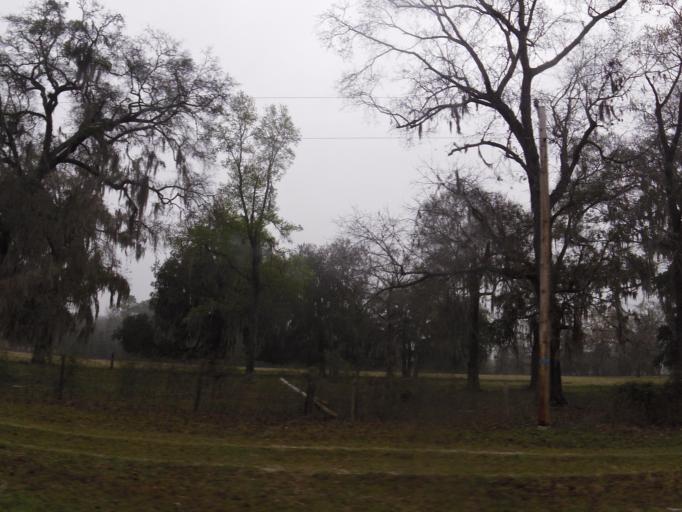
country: US
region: Florida
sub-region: Alachua County
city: Alachua
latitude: 29.8968
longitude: -82.4448
